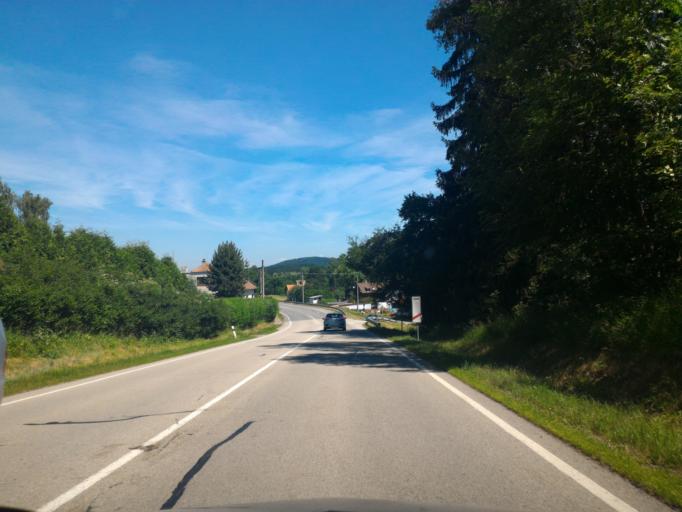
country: CZ
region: Vysocina
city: Dolni Cerekev
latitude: 49.3282
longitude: 15.4834
